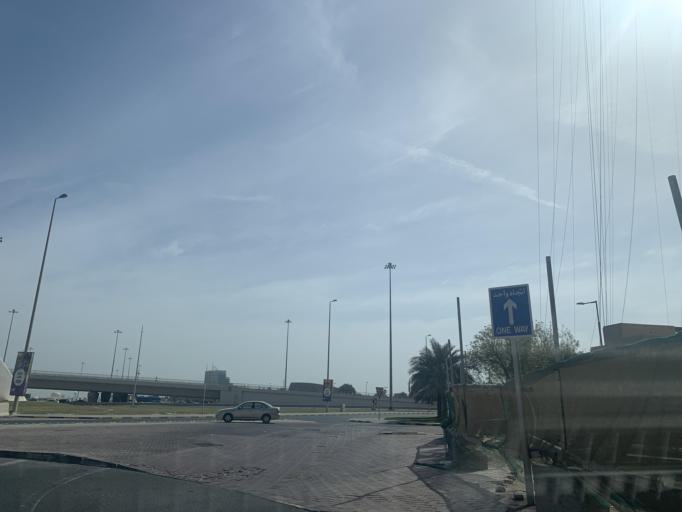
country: BH
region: Muharraq
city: Al Muharraq
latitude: 26.2404
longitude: 50.5932
